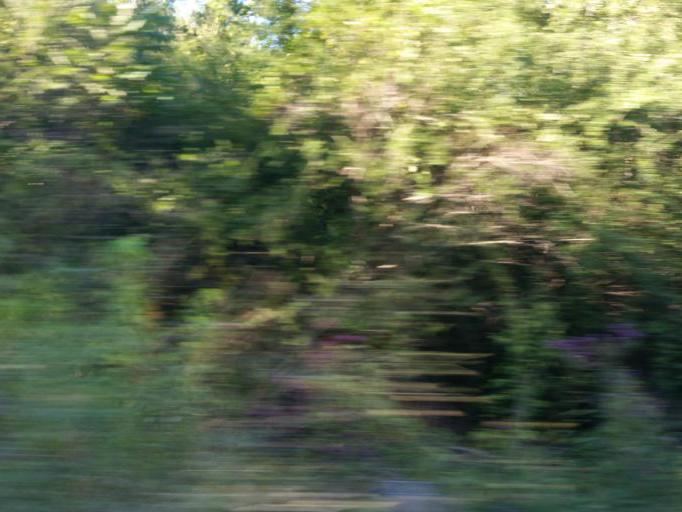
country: US
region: Tennessee
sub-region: Knox County
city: Knoxville
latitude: 35.9081
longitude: -83.9399
